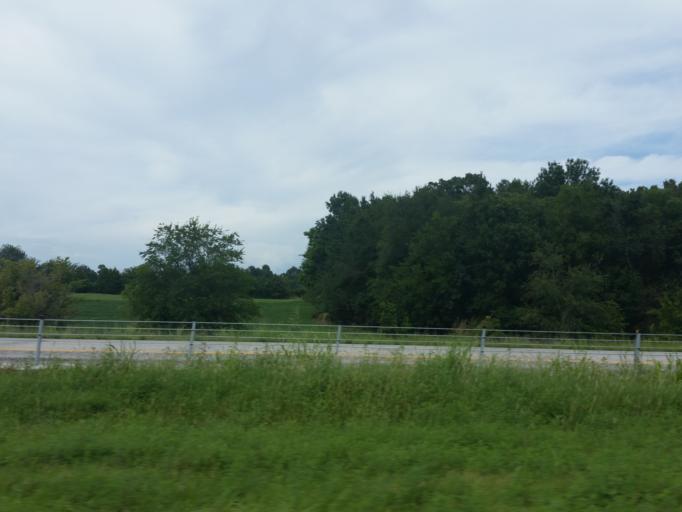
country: US
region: Kentucky
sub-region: Trigg County
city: Cadiz
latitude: 36.9217
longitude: -87.7997
